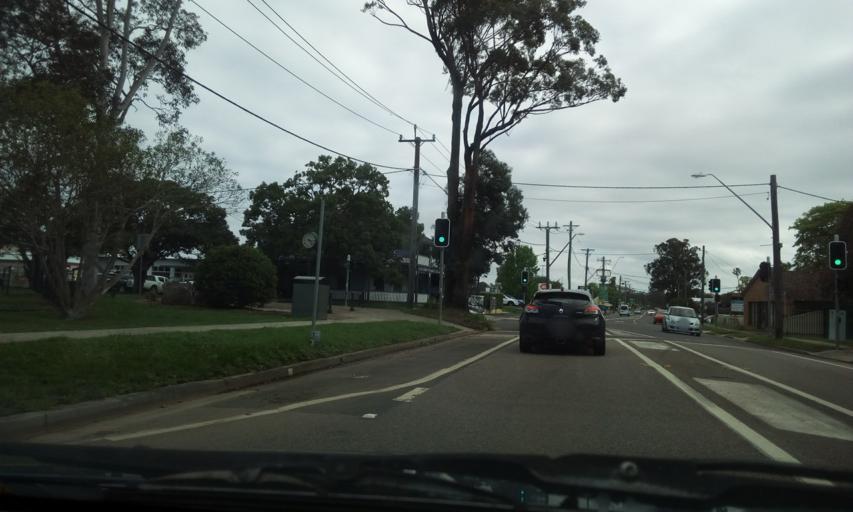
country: AU
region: New South Wales
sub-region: Wollondilly
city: Douglas Park
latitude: -34.1991
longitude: 150.7882
